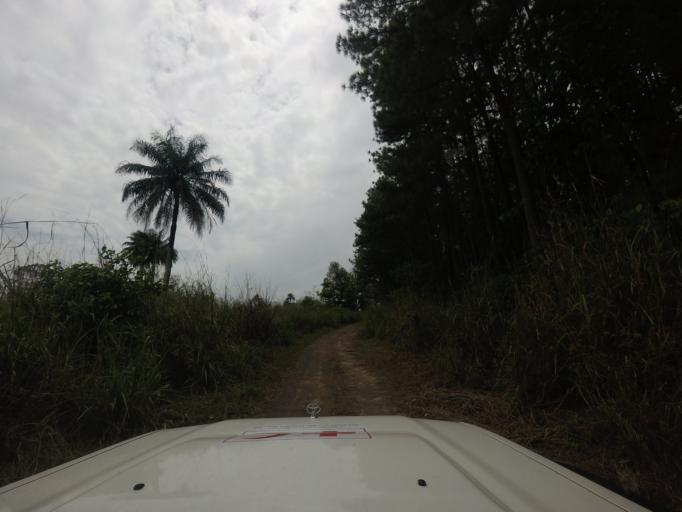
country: GN
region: Nzerekore
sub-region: Prefecture de Guekedou
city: Gueckedou
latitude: 8.4295
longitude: -10.2420
